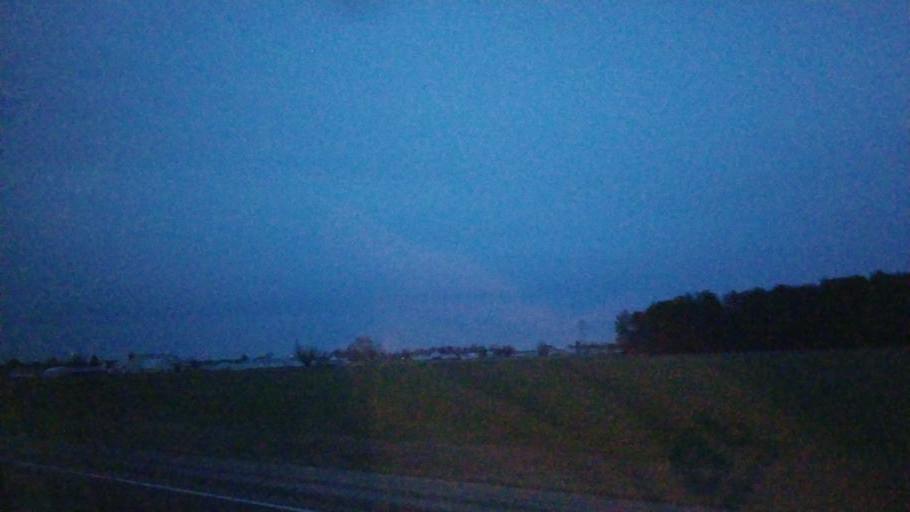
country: US
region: Indiana
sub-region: Adams County
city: Berne
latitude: 40.6896
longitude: -84.9559
